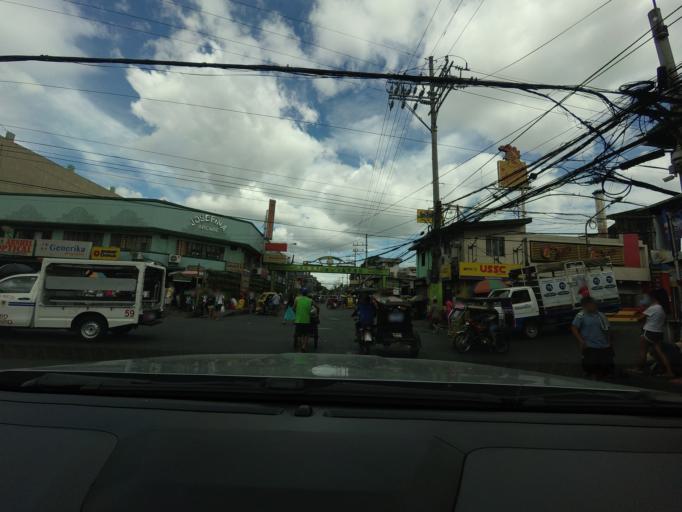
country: PH
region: Calabarzon
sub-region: Province of Rizal
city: Pateros
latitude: 14.5575
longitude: 121.0845
